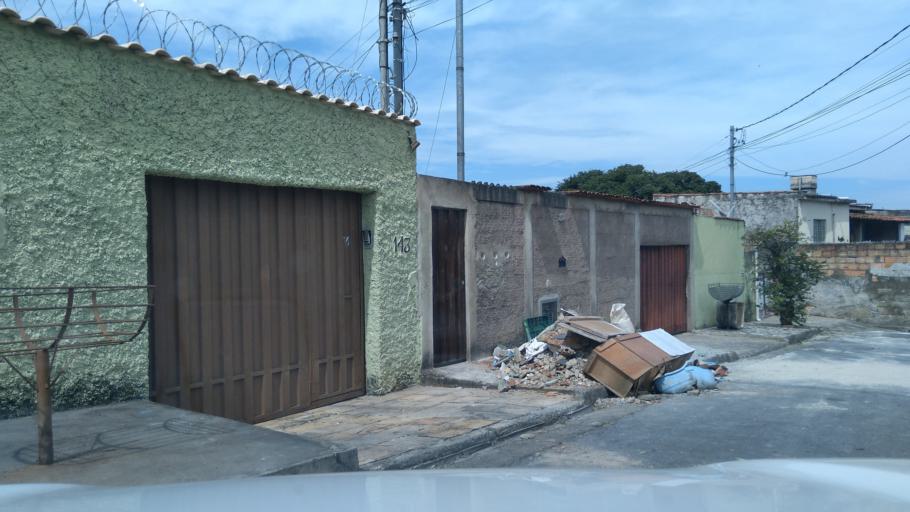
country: BR
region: Minas Gerais
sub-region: Contagem
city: Contagem
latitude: -19.8980
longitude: -44.0079
